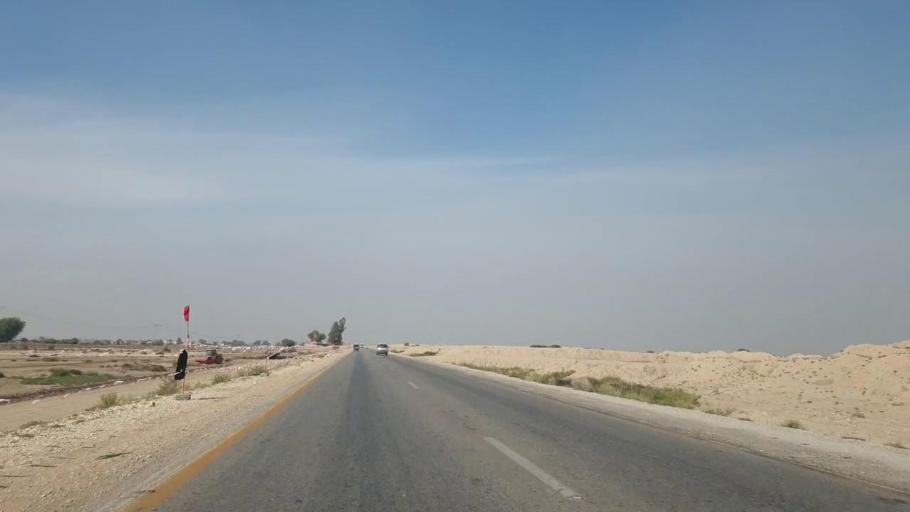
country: PK
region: Sindh
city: Sann
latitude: 25.9603
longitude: 68.1924
